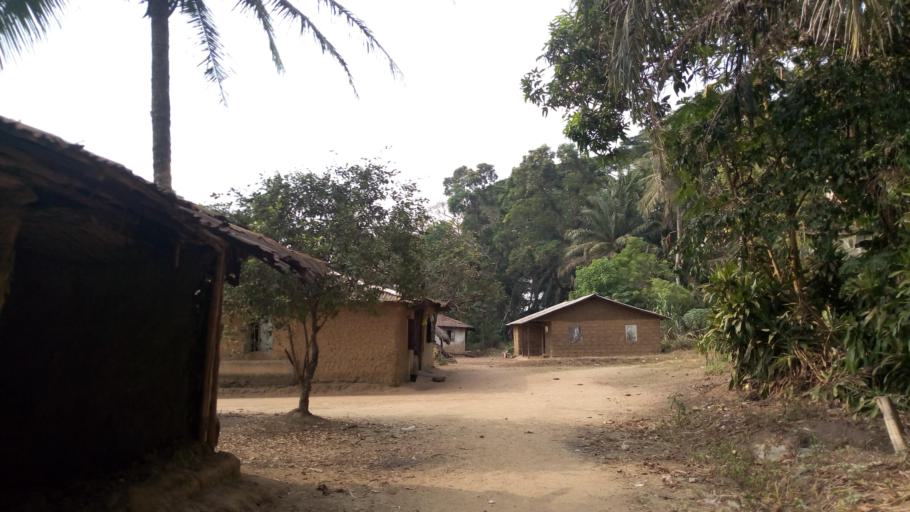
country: SL
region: Southern Province
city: Mogbwemo
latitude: 7.7658
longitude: -12.3083
